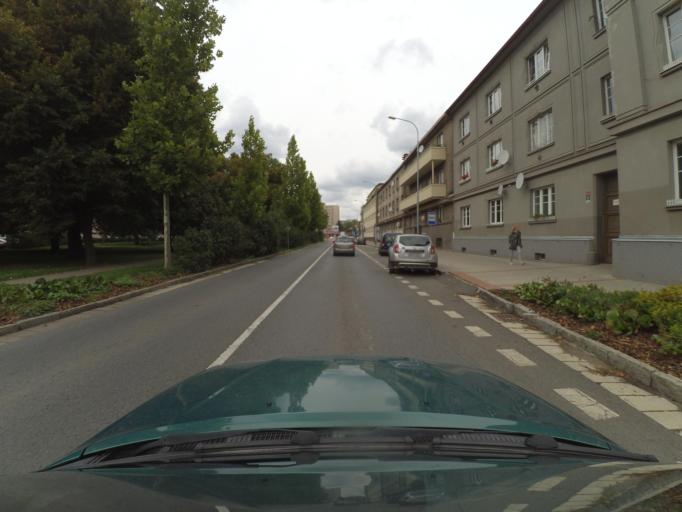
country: CZ
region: Central Bohemia
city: Rakovnik
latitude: 50.1028
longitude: 13.7292
